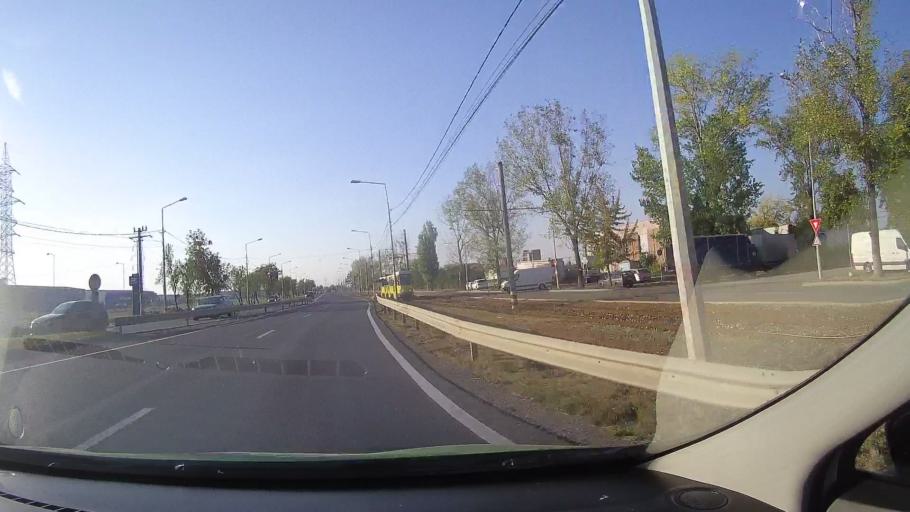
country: RO
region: Bihor
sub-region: Comuna Santandrei
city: Santandrei
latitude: 47.0827
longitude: 21.8886
